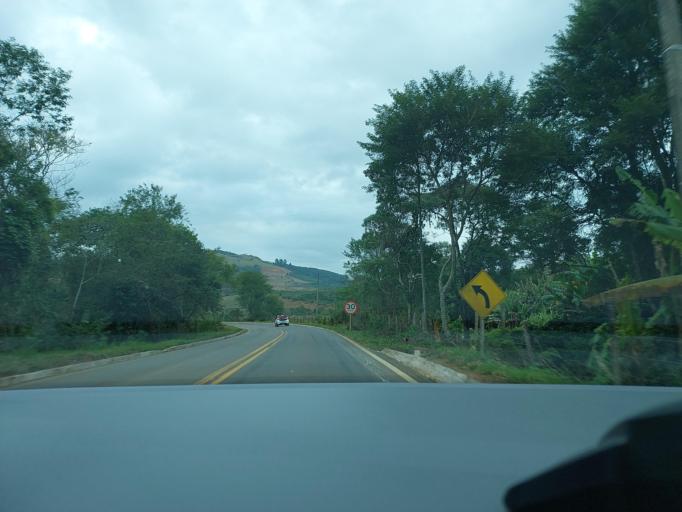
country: BR
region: Minas Gerais
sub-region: Mirai
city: Mirai
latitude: -20.9801
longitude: -42.5871
